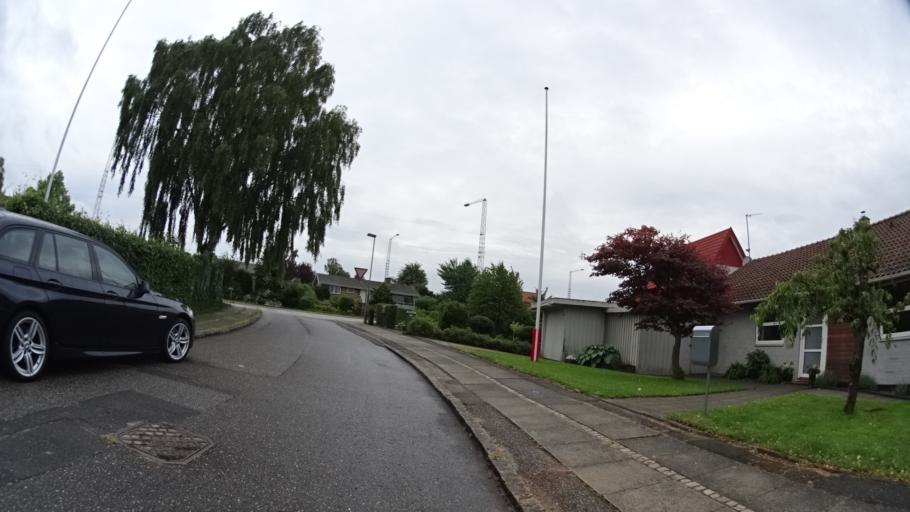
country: DK
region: Central Jutland
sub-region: Arhus Kommune
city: Arhus
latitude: 56.1249
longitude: 10.1803
